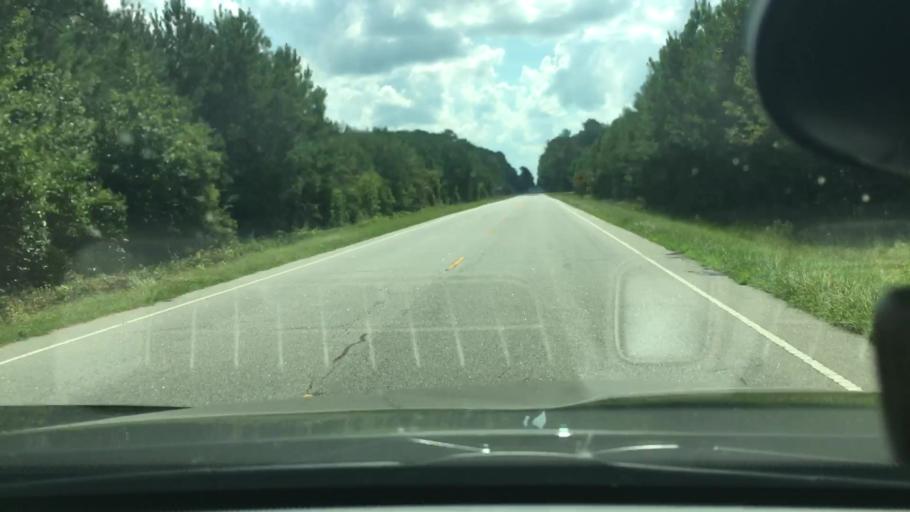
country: US
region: North Carolina
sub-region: Edgecombe County
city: Pinetops
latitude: 35.7629
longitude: -77.5601
